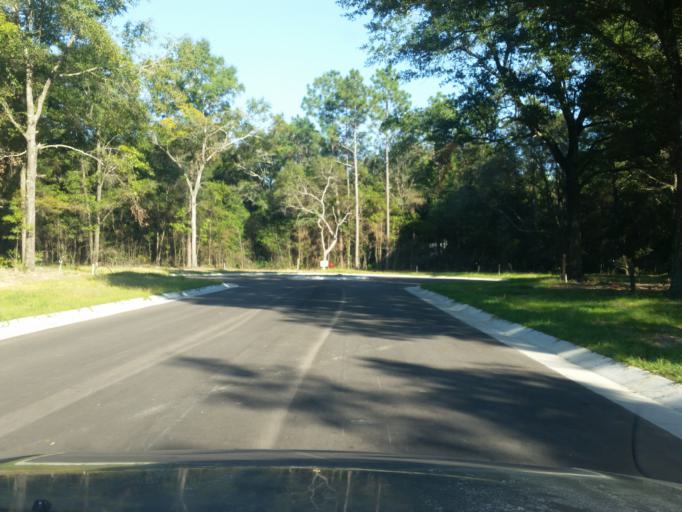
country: US
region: Florida
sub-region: Escambia County
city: Ferry Pass
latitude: 30.5017
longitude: -87.1993
